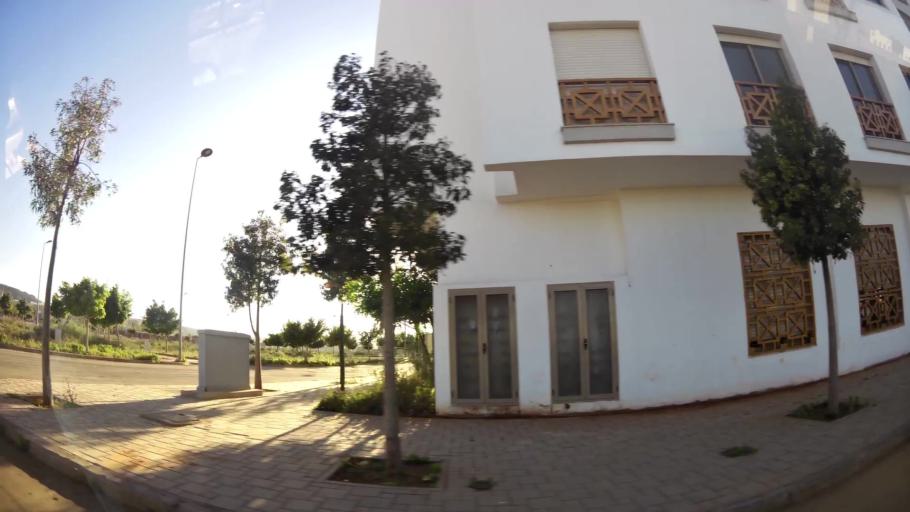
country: MA
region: Oriental
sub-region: Berkane-Taourirt
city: Madagh
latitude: 35.0849
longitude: -2.2528
